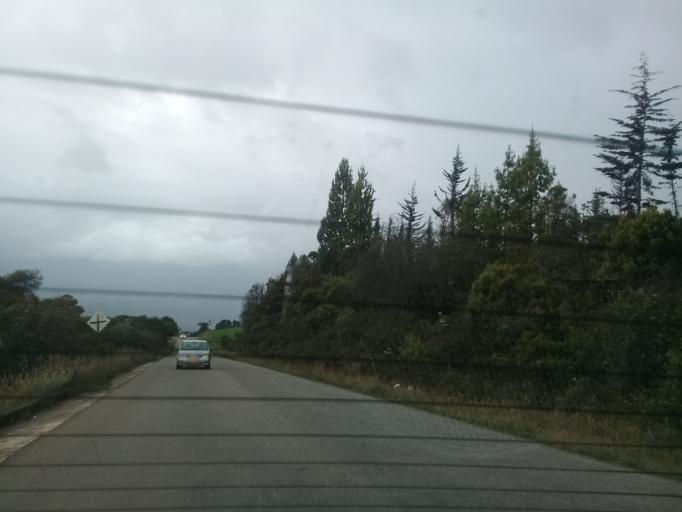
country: CO
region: Cundinamarca
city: Junin
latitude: 4.8447
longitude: -73.7456
